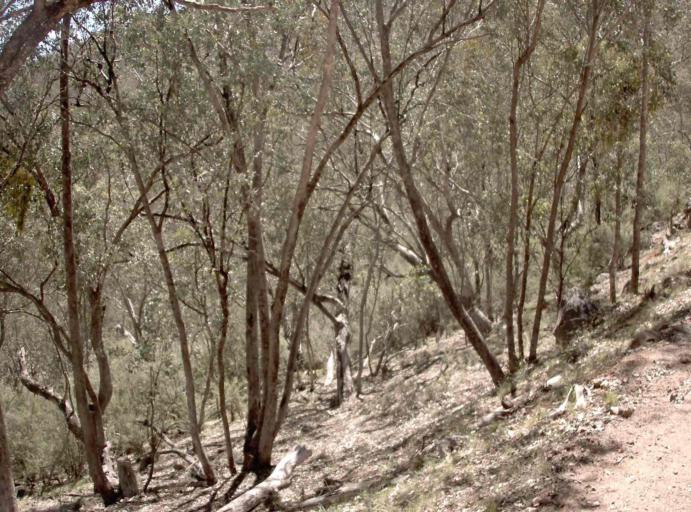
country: AU
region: New South Wales
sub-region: Snowy River
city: Jindabyne
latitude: -37.0591
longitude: 148.5299
